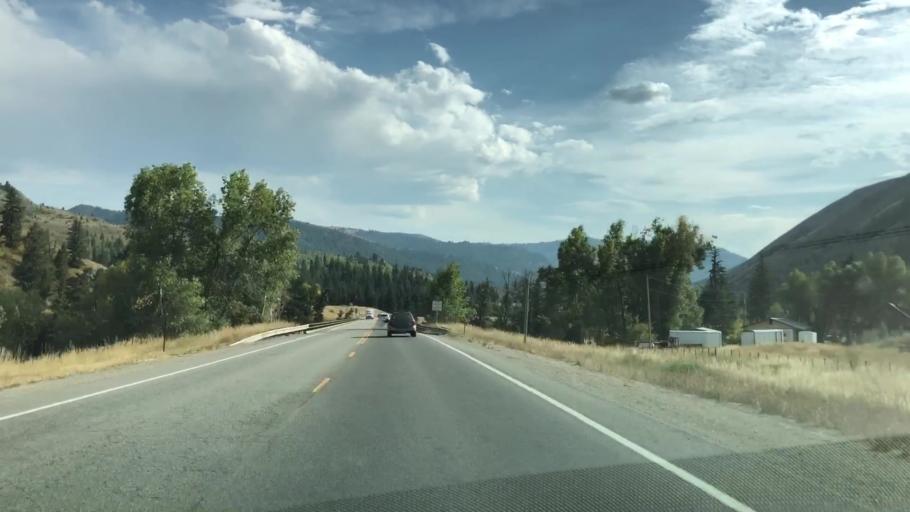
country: US
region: Wyoming
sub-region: Teton County
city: Hoback
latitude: 43.3456
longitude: -110.7222
